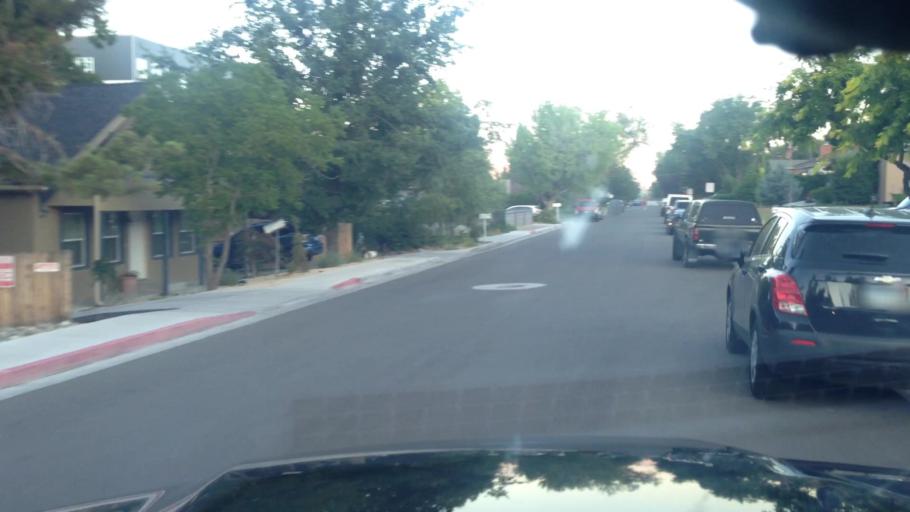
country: US
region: Nevada
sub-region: Washoe County
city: Reno
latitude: 39.5446
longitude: -119.8210
